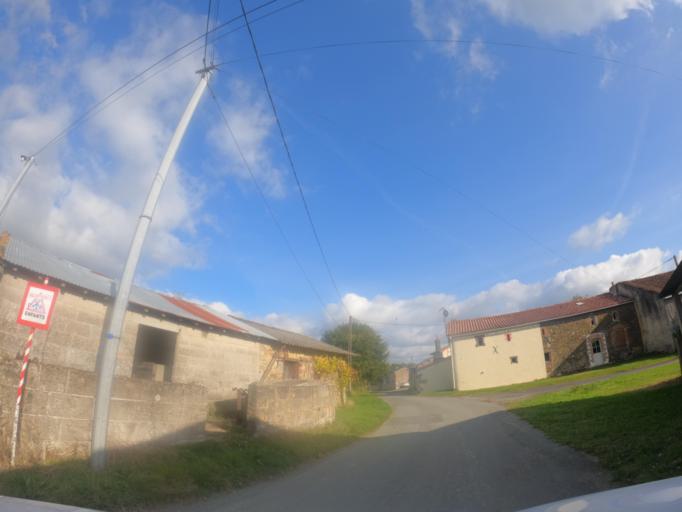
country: FR
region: Poitou-Charentes
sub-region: Departement des Deux-Sevres
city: La Foret-sur-Sevre
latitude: 46.7821
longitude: -0.6160
